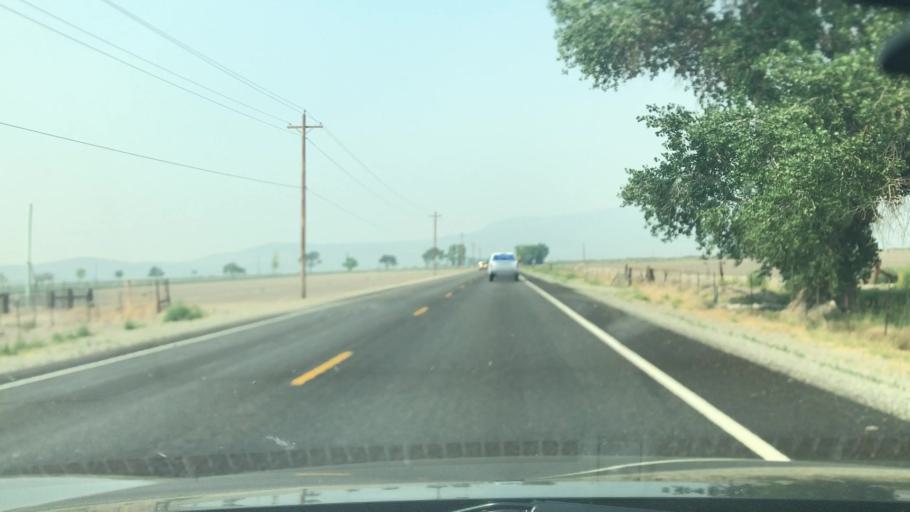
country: US
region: Nevada
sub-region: Lyon County
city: Yerington
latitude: 39.1242
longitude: -119.1810
